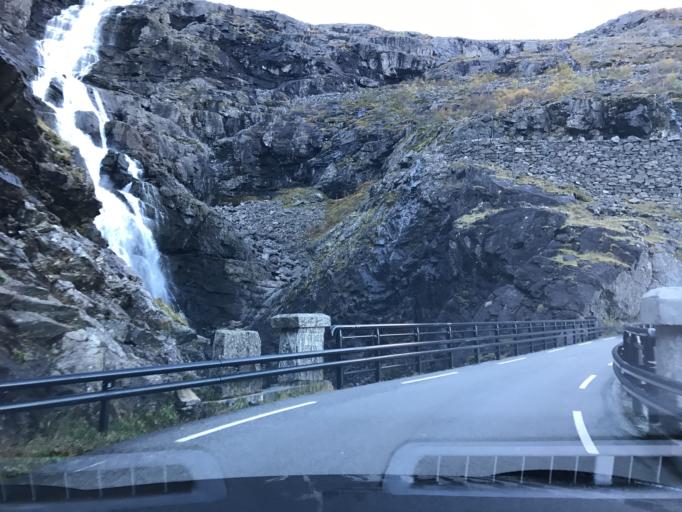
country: NO
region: More og Romsdal
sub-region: Rauma
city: Andalsnes
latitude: 62.4568
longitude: 7.6742
